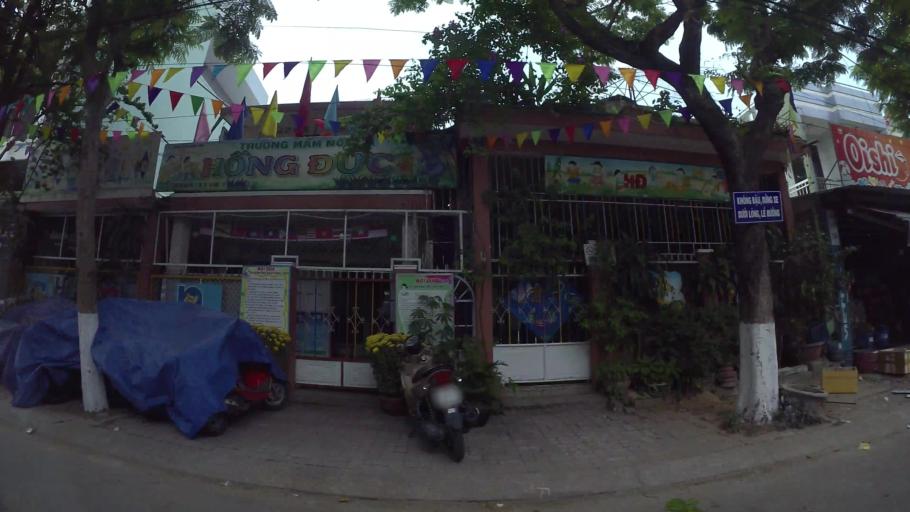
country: VN
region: Da Nang
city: Son Tra
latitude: 16.1000
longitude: 108.2544
